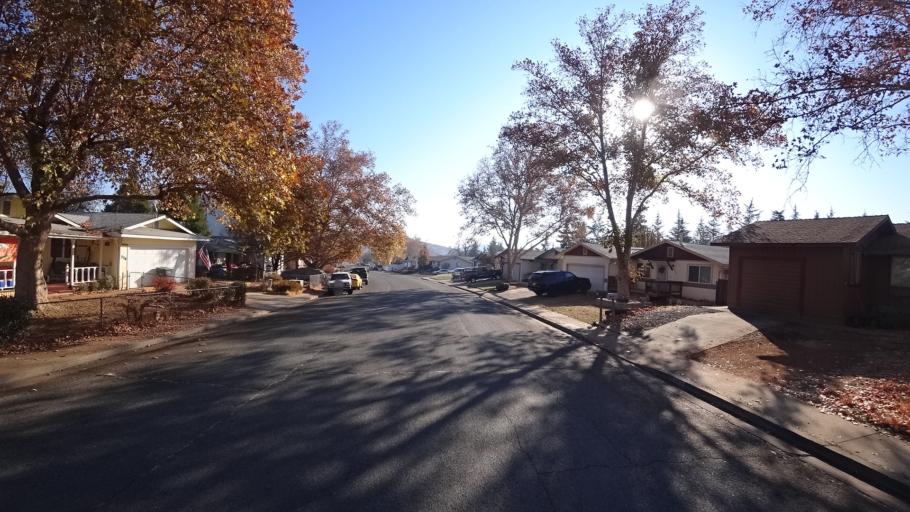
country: US
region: California
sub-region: Siskiyou County
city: Yreka
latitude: 41.7211
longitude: -122.6461
